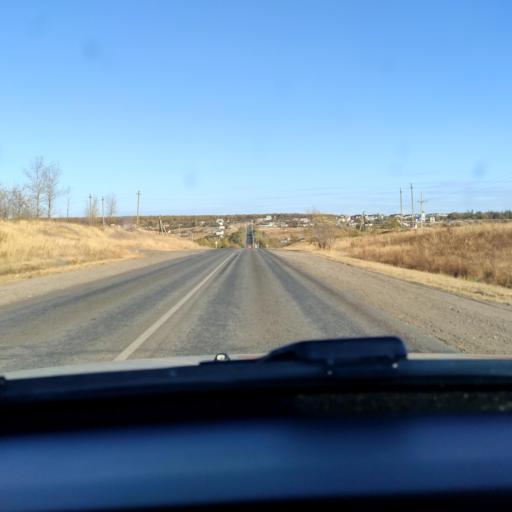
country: RU
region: Voronezj
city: Semiluki
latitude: 51.7252
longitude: 39.0092
